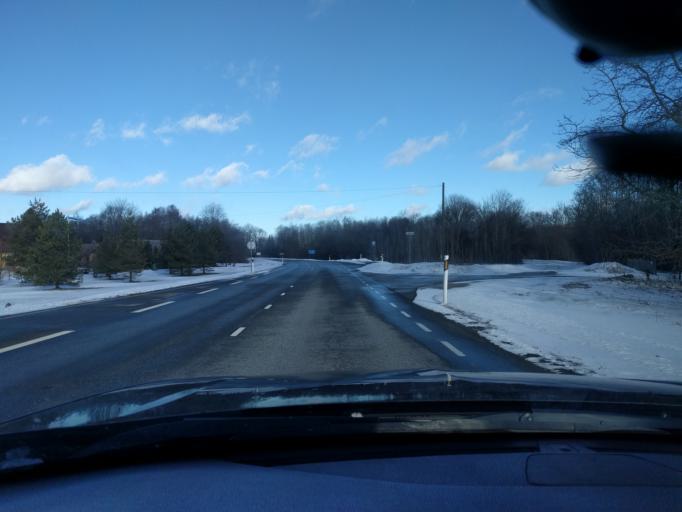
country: EE
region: Harju
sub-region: Raasiku vald
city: Raasiku
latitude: 59.3825
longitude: 25.1959
